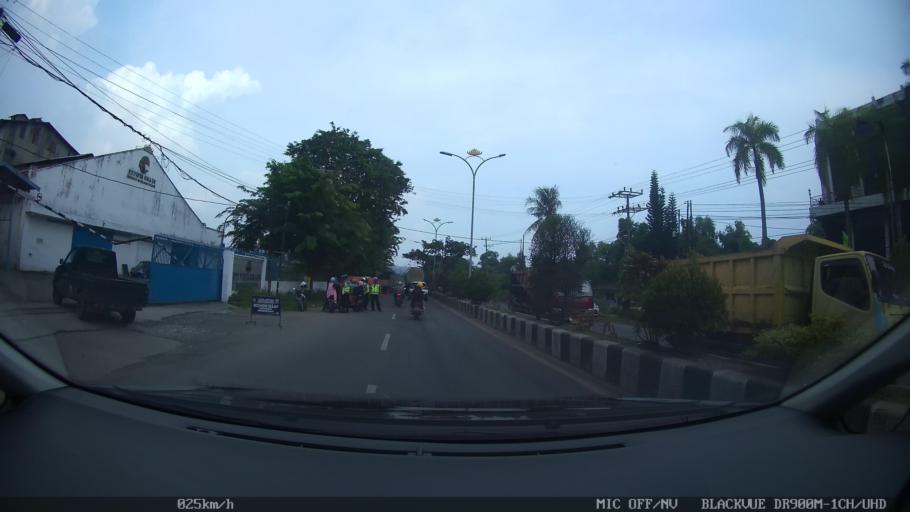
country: ID
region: Lampung
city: Panjang
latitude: -5.4454
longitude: 105.2961
